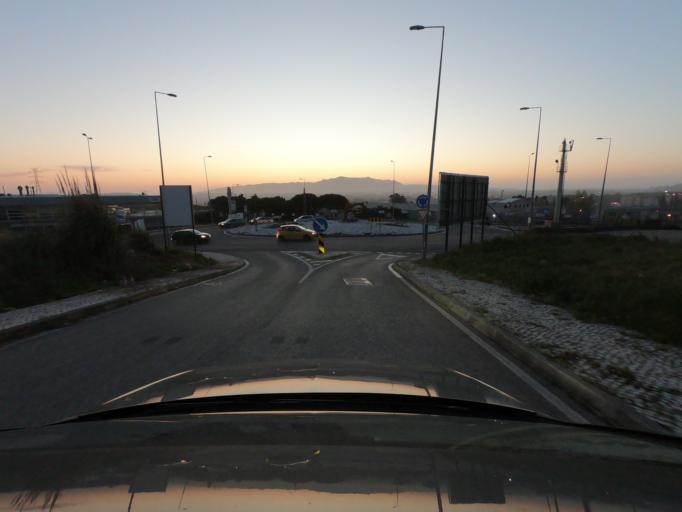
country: PT
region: Lisbon
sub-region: Sintra
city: Cacem
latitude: 38.7583
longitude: -9.3065
